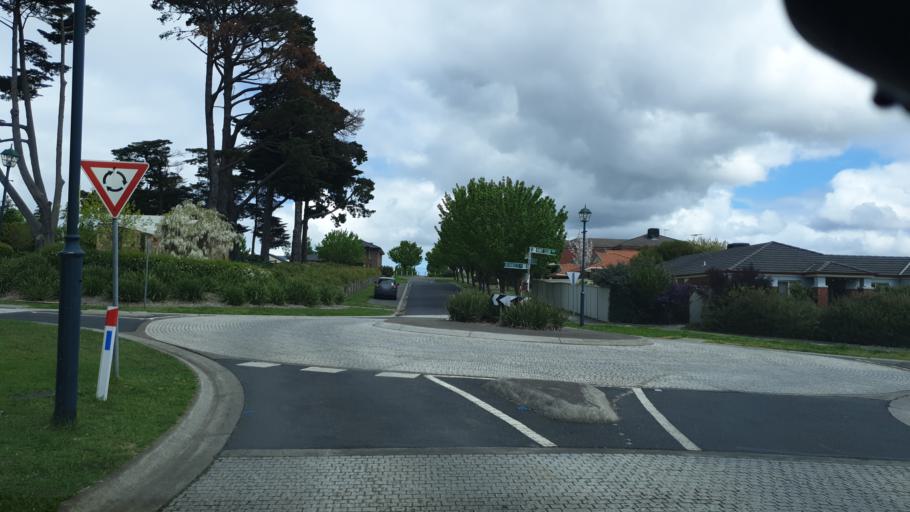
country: AU
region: Victoria
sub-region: Casey
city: Cranbourne East
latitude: -38.1052
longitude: 145.2988
